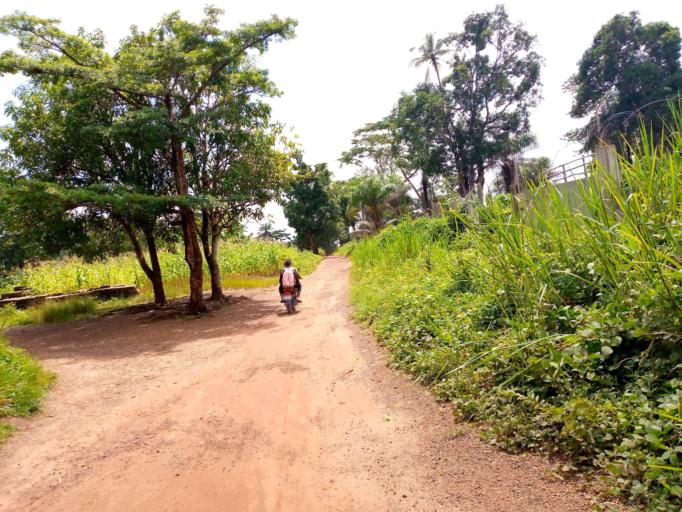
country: SL
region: Northern Province
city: Magburaka
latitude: 8.7092
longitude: -11.9281
